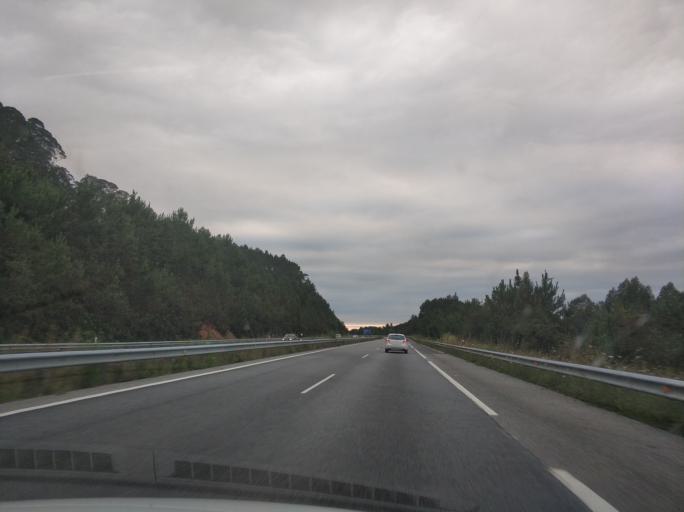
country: ES
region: Asturias
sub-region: Province of Asturias
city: Tineo
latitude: 43.5431
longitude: -6.4308
